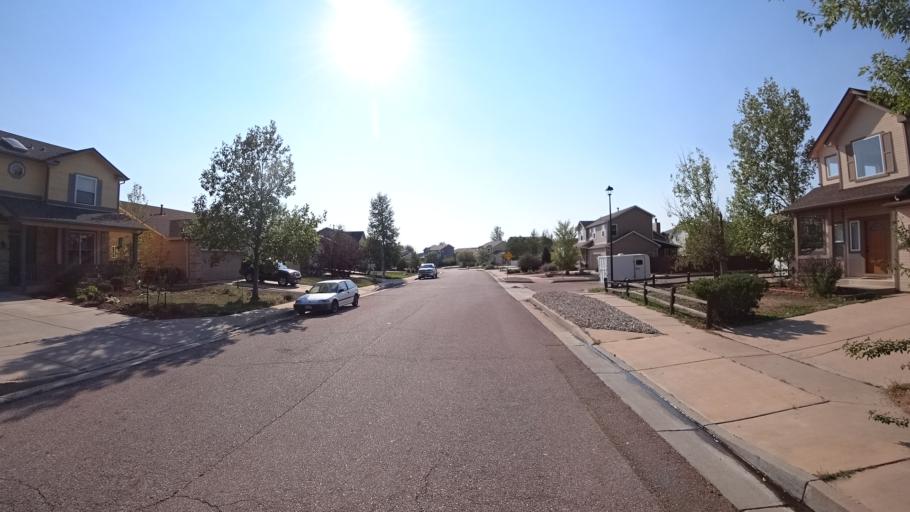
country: US
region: Colorado
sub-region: El Paso County
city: Stratmoor
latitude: 38.7685
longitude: -104.8025
